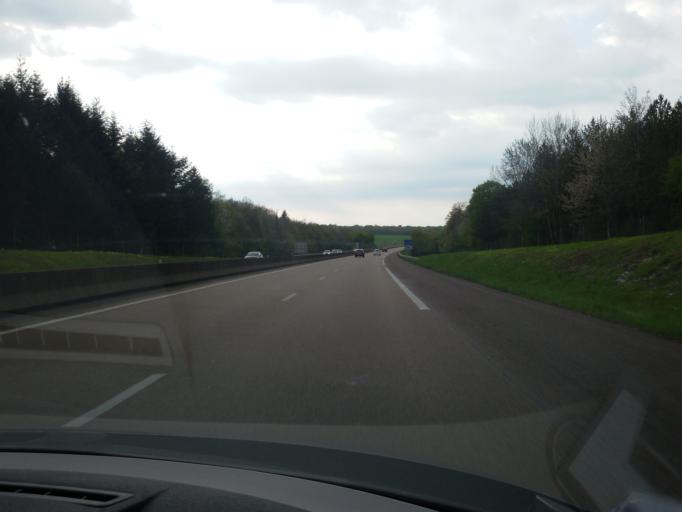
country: FR
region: Champagne-Ardenne
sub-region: Departement de la Haute-Marne
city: Rolampont
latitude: 47.9528
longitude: 5.1636
